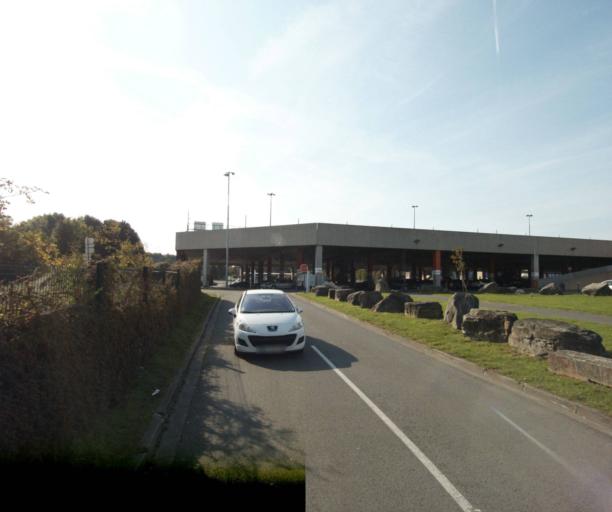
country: FR
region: Nord-Pas-de-Calais
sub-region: Departement du Nord
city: Lomme
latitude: 50.6518
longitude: 2.9800
